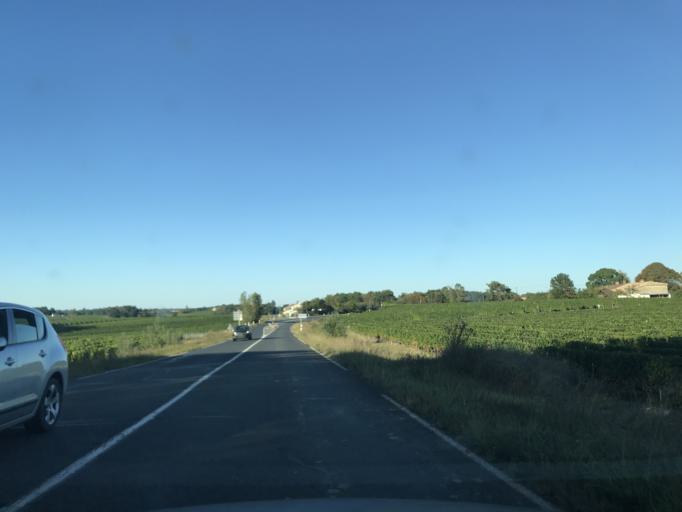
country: FR
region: Aquitaine
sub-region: Departement de la Gironde
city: Sauveterre-de-Guyenne
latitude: 44.6481
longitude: -0.1241
